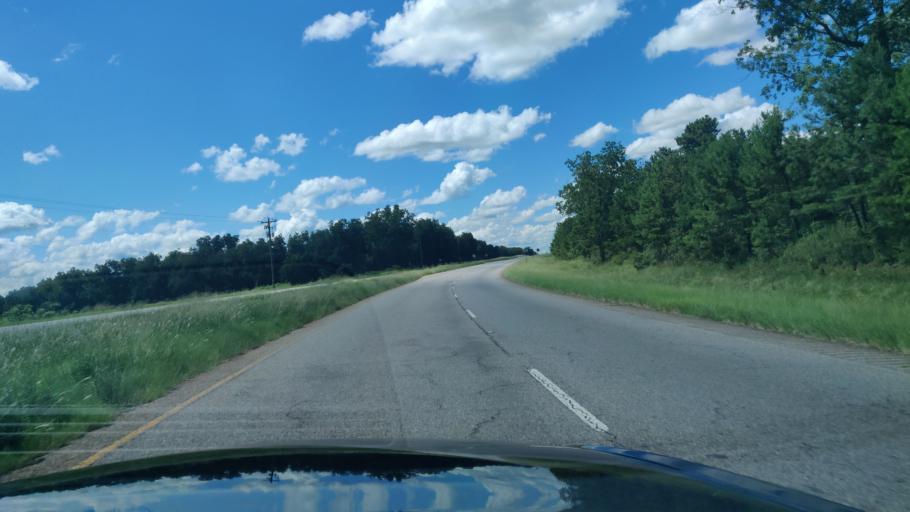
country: US
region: Georgia
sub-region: Stewart County
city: Richland
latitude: 32.0287
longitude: -84.6735
